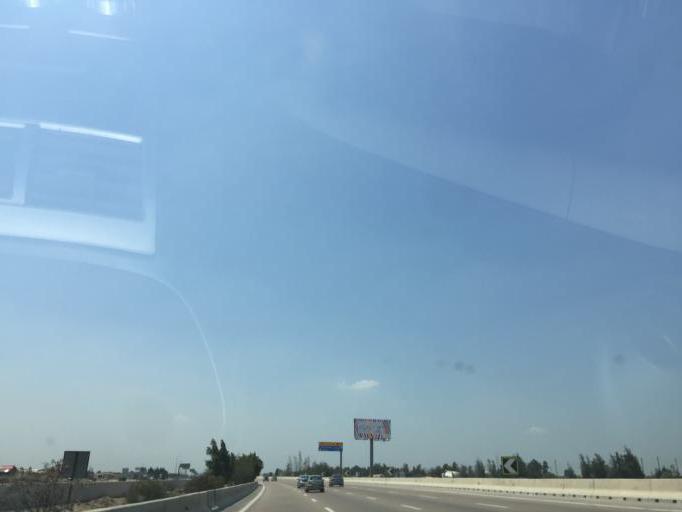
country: EG
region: Al Buhayrah
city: Beheira
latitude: 30.4413
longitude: 30.3283
